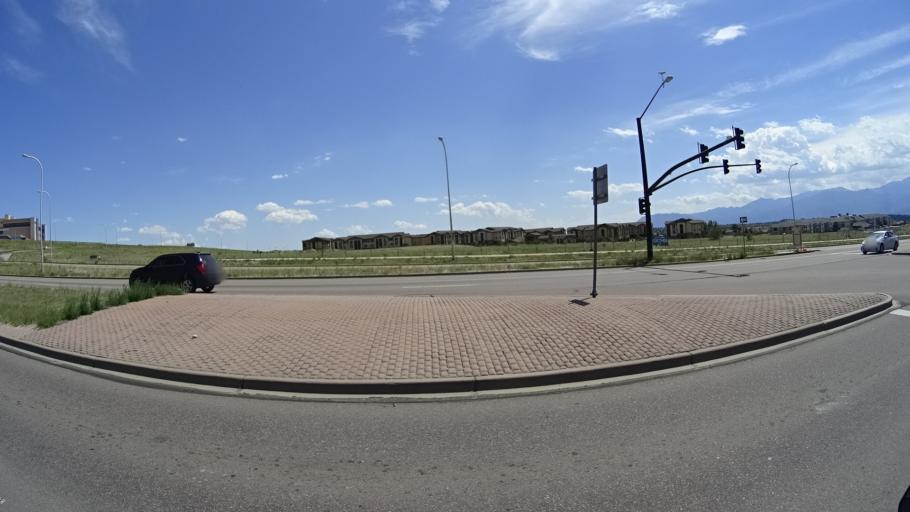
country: US
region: Colorado
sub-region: El Paso County
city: Black Forest
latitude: 38.9403
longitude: -104.7223
